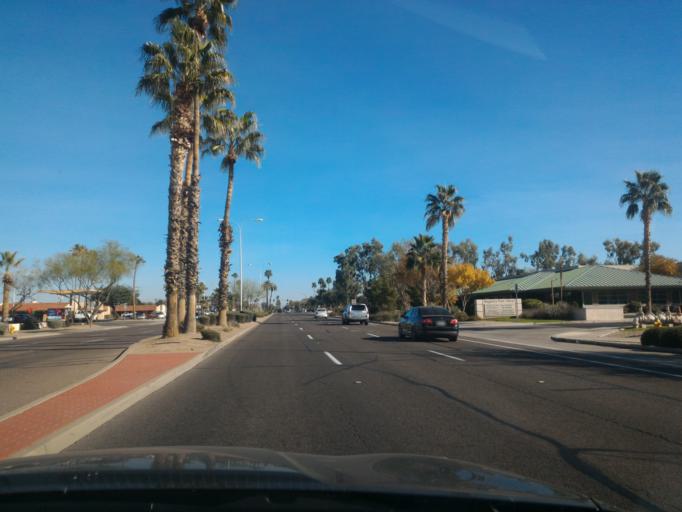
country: US
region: Arizona
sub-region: Maricopa County
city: Chandler
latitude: 33.3060
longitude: -111.8670
